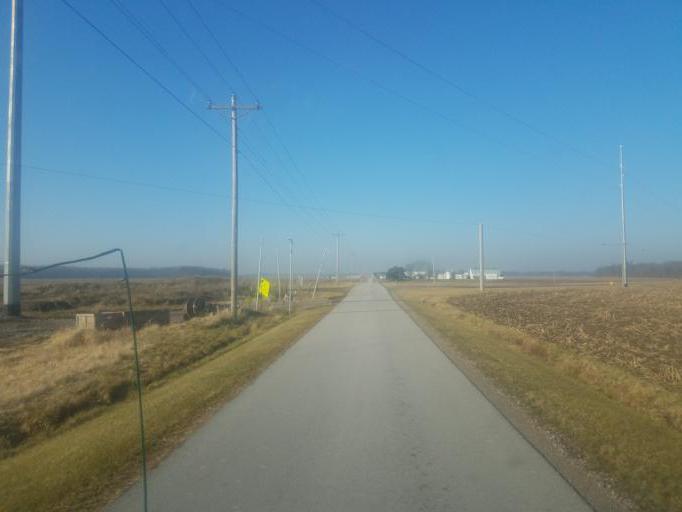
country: US
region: Ohio
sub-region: Crawford County
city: Bucyrus
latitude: 41.0082
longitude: -82.9356
